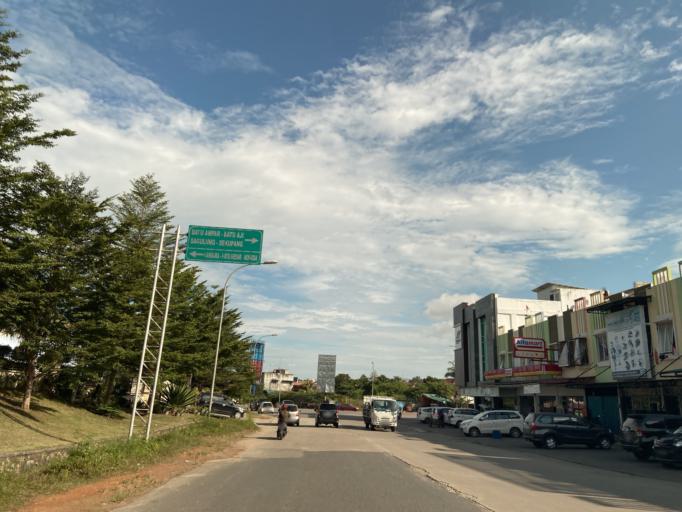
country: SG
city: Singapore
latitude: 1.1078
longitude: 104.0792
